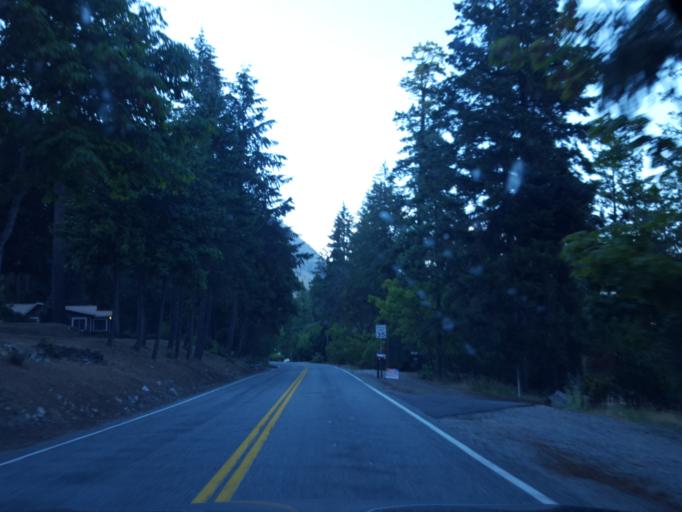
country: US
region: Washington
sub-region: Chelan County
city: Granite Falls
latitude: 47.9250
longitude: -120.2105
